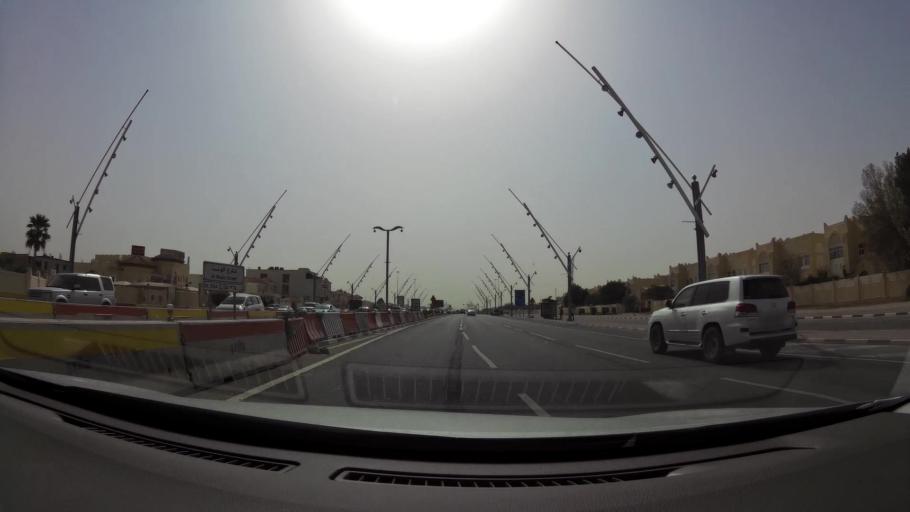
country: QA
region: Baladiyat ar Rayyan
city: Ar Rayyan
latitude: 25.2661
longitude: 51.4668
